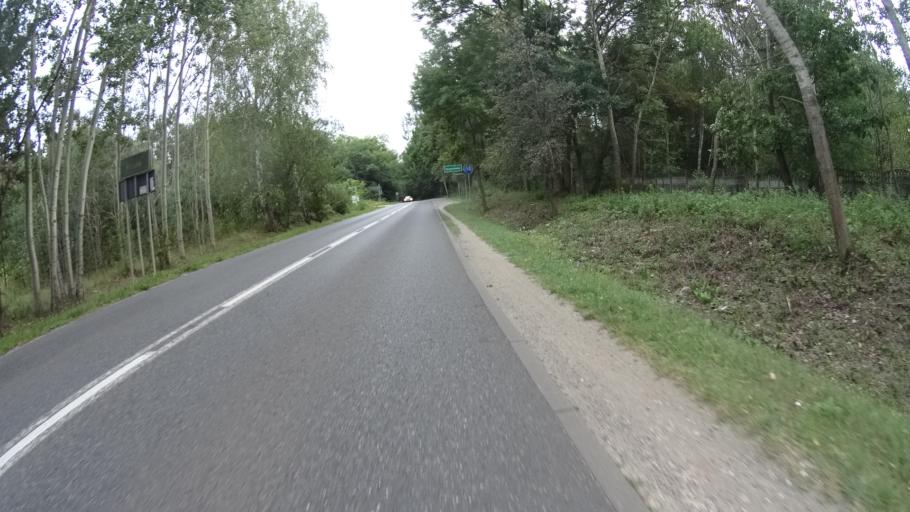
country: PL
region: Masovian Voivodeship
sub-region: Powiat pruszkowski
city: Granica
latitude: 52.1244
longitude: 20.7986
